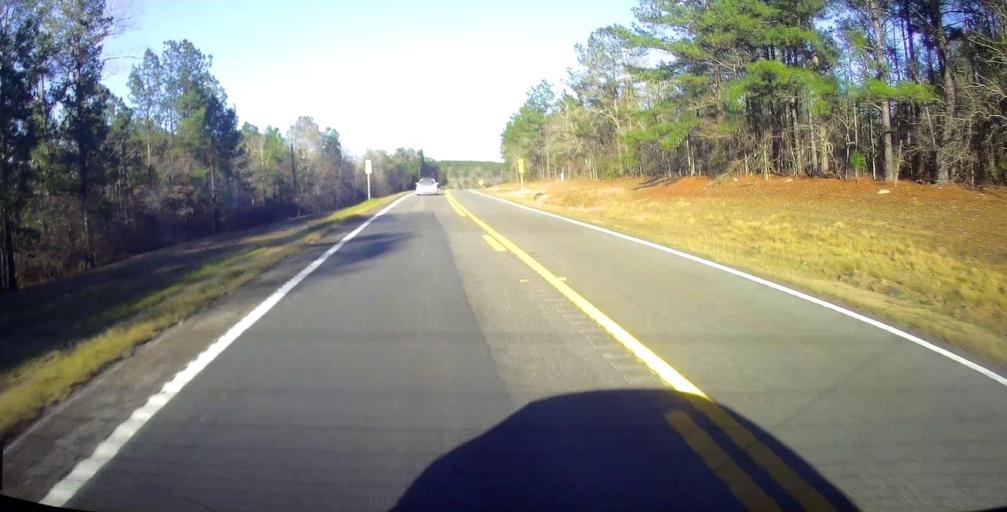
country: US
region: Georgia
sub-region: Taylor County
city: Butler
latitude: 32.5219
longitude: -84.3168
